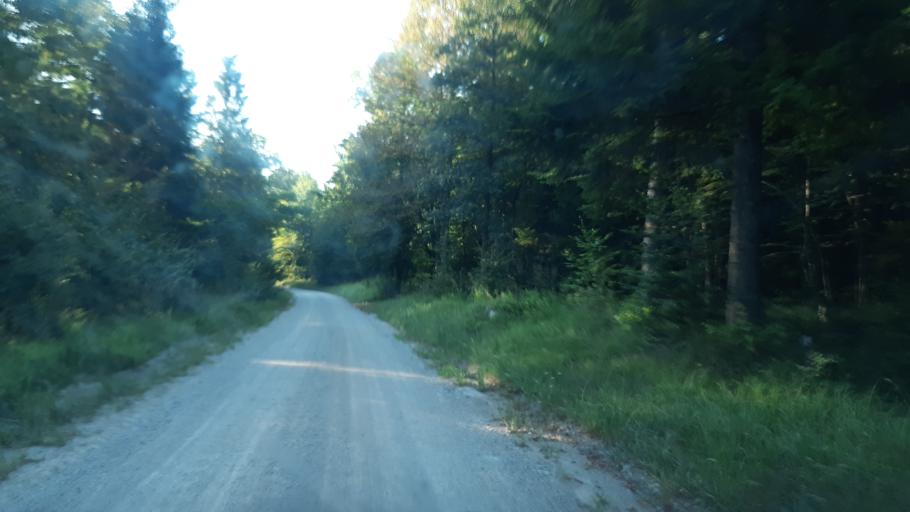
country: SI
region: Kocevje
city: Kocevje
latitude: 45.6667
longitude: 14.9368
